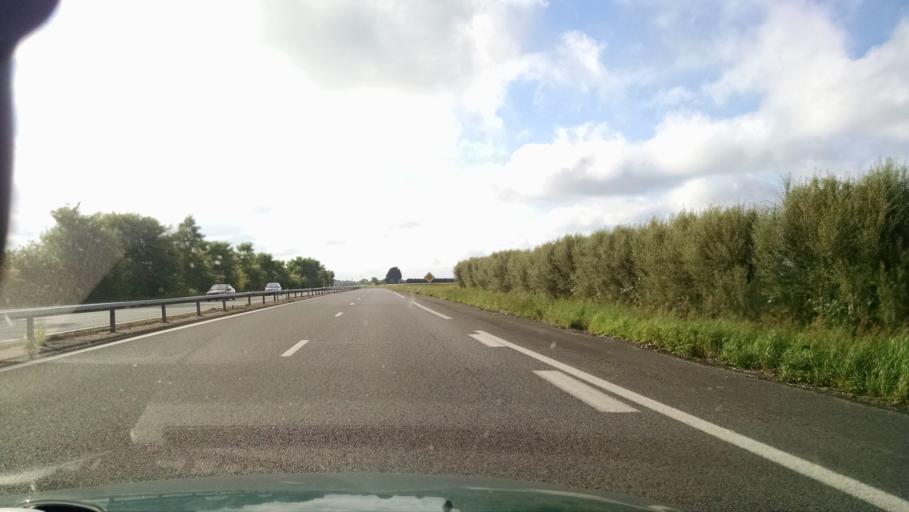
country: FR
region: Brittany
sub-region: Departement du Finistere
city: Henvic
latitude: 48.6230
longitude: -3.9050
